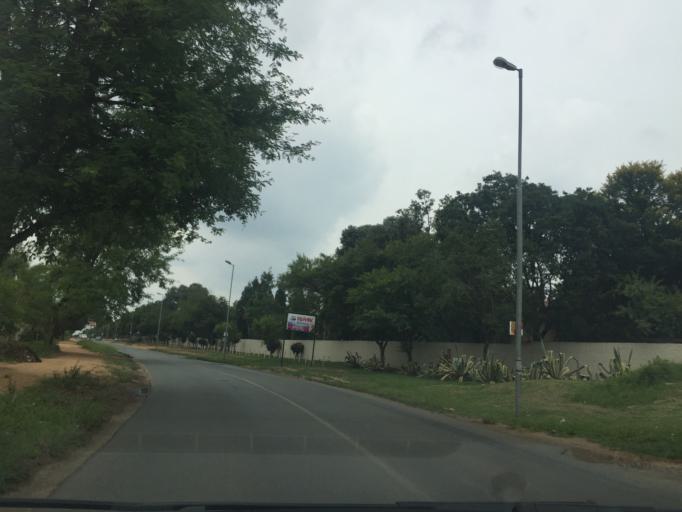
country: ZA
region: Gauteng
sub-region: City of Johannesburg Metropolitan Municipality
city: Diepsloot
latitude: -26.0184
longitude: 27.9989
